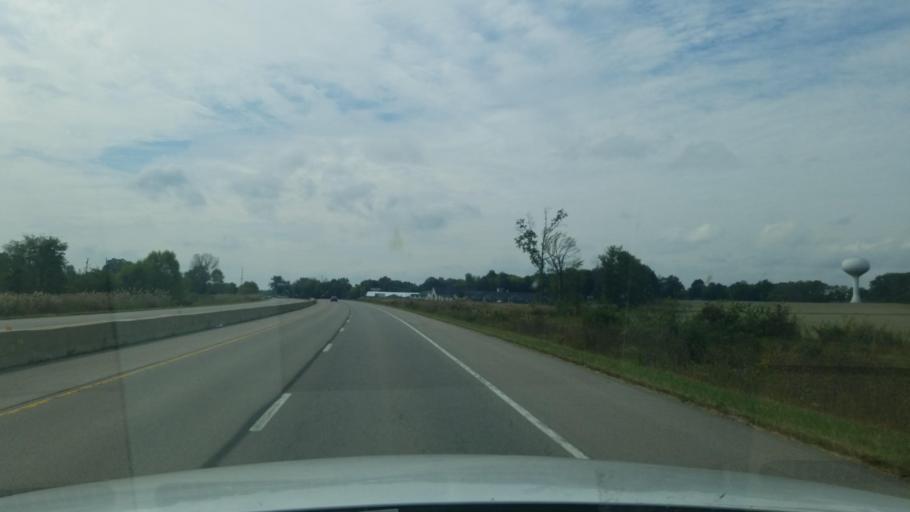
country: US
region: Illinois
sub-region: Saline County
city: Harrisburg
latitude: 37.7415
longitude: -88.5580
